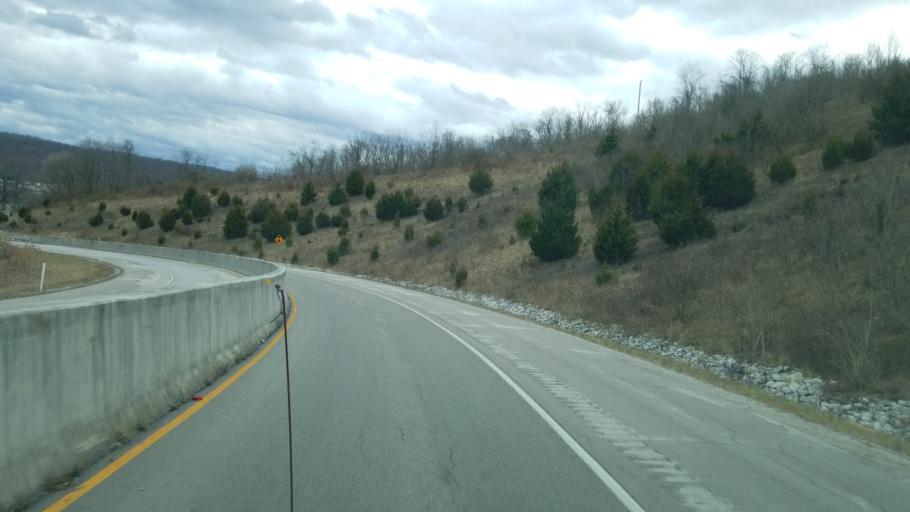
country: US
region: Ohio
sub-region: Brown County
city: Aberdeen
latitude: 38.6820
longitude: -83.7888
